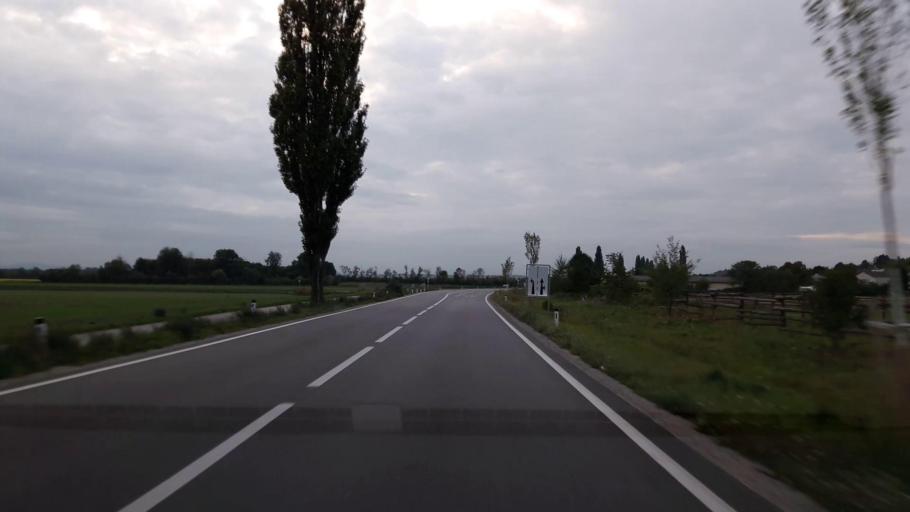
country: AT
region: Lower Austria
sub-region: Politischer Bezirk Bruck an der Leitha
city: Trautmannsdorf an der Leitha
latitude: 48.0519
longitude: 16.6408
